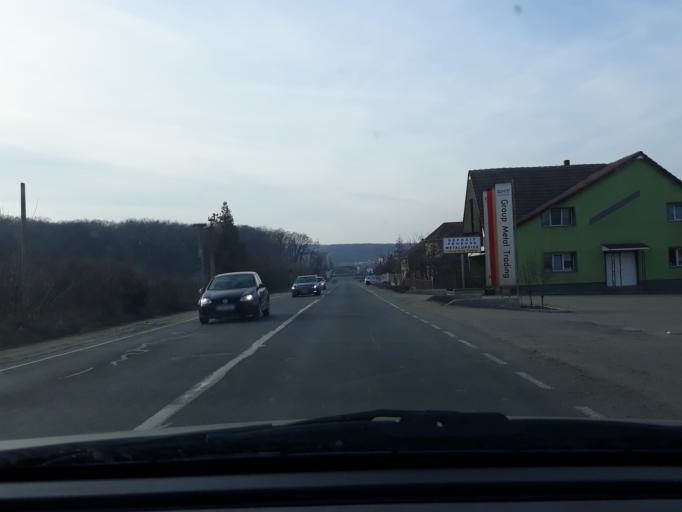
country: RO
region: Salaj
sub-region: Comuna Hereclean
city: Hereclean
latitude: 47.2250
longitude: 23.0148
